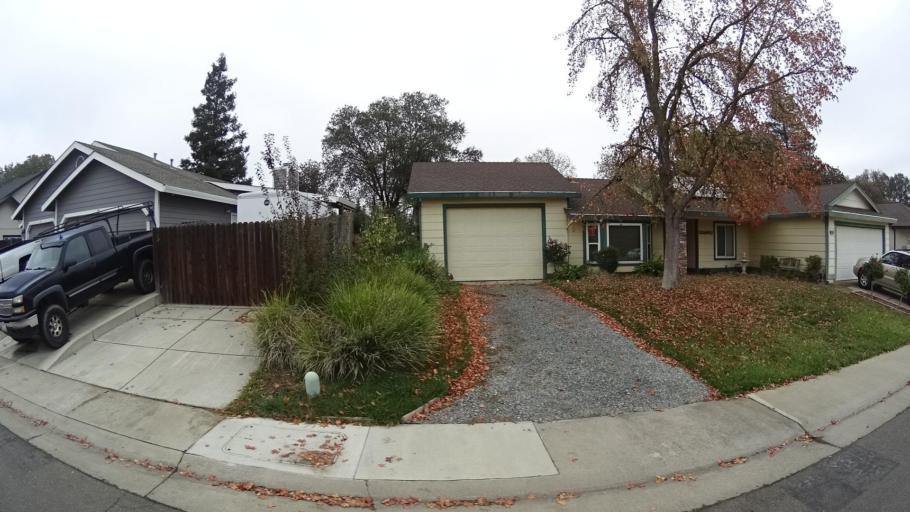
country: US
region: California
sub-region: Sacramento County
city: Elk Grove
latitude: 38.4007
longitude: -121.3626
